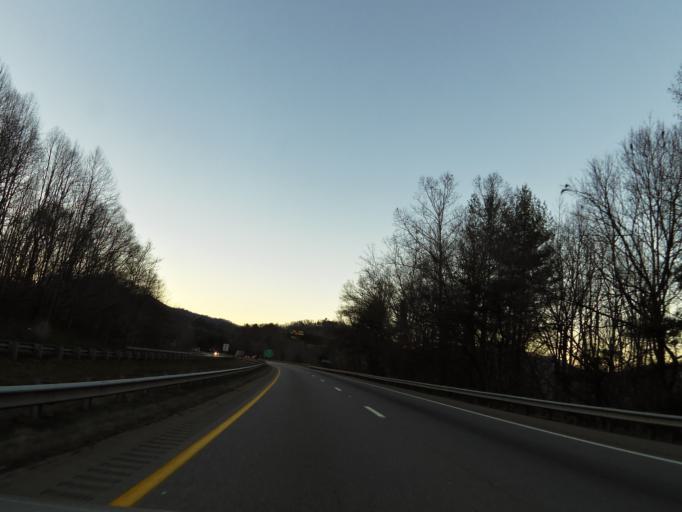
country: US
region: North Carolina
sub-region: Haywood County
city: Lake Junaluska
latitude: 35.5655
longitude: -82.9523
